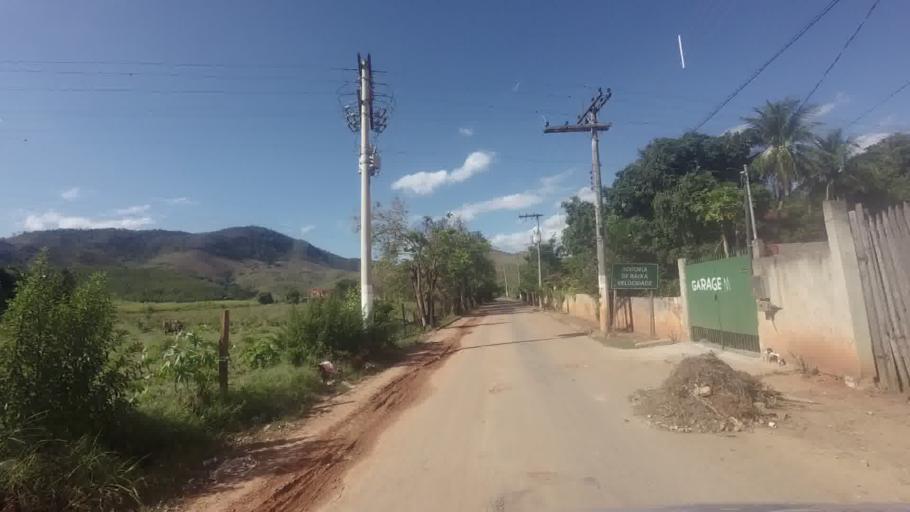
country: BR
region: Rio de Janeiro
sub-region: Bom Jesus Do Itabapoana
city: Bom Jesus do Itabapoana
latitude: -21.1228
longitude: -41.6638
